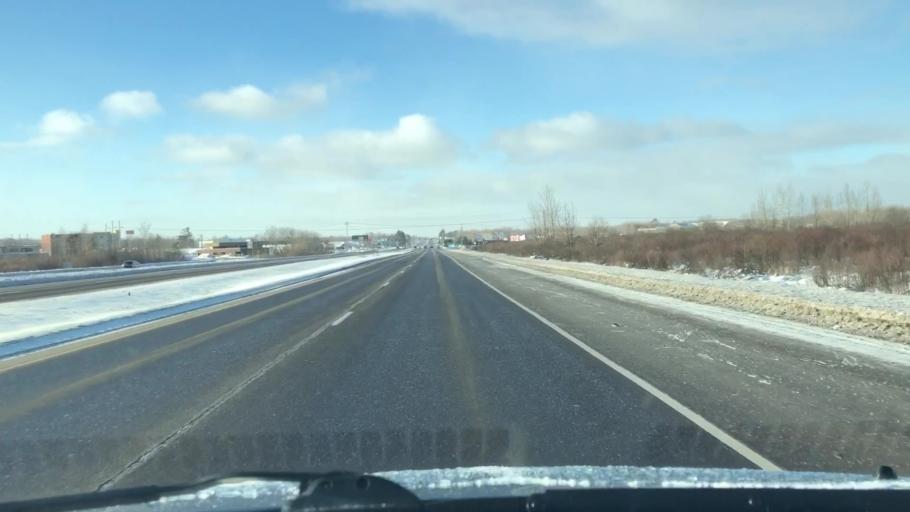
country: US
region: Minnesota
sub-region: Saint Louis County
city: Hermantown
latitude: 46.8117
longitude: -92.1695
